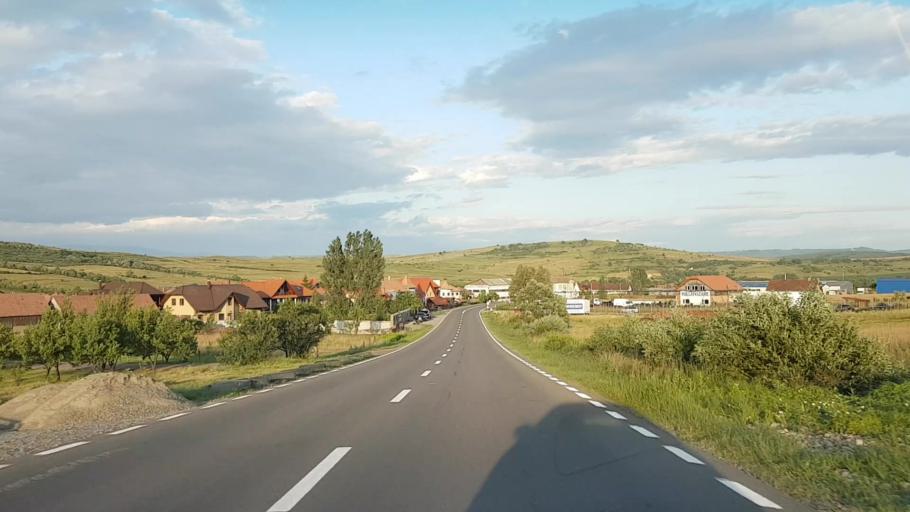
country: RO
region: Harghita
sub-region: Comuna Lupeni
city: Lupeni
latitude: 46.3708
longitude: 25.2262
